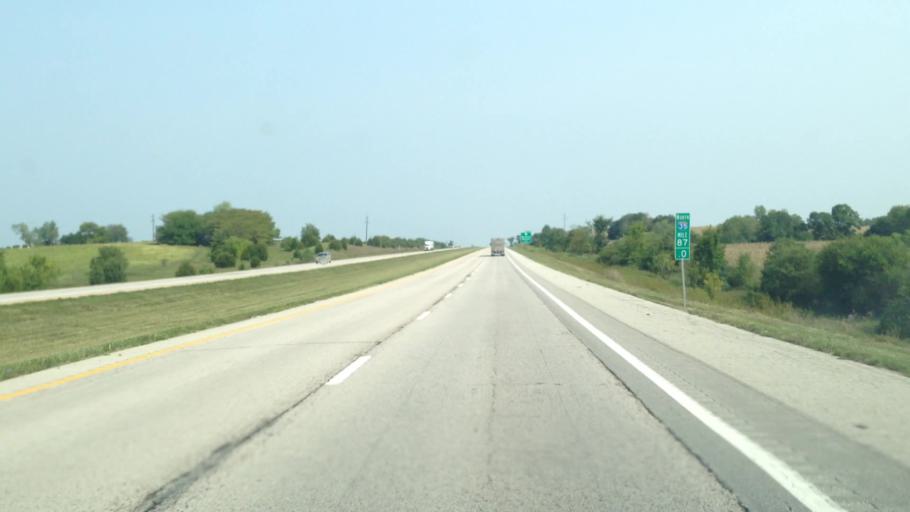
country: US
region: Missouri
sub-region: Harrison County
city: Bethany
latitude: 40.1896
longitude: -94.0143
